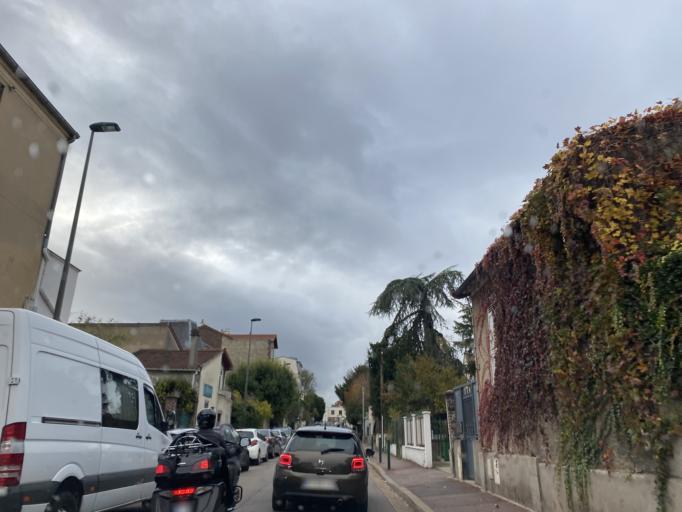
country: FR
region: Ile-de-France
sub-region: Departement des Hauts-de-Seine
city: Suresnes
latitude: 48.8761
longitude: 2.2229
